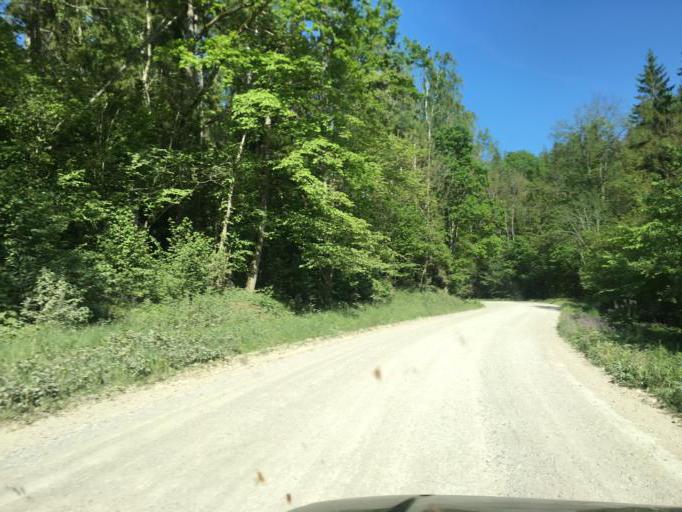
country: LV
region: Dundaga
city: Dundaga
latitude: 57.6085
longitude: 22.4723
